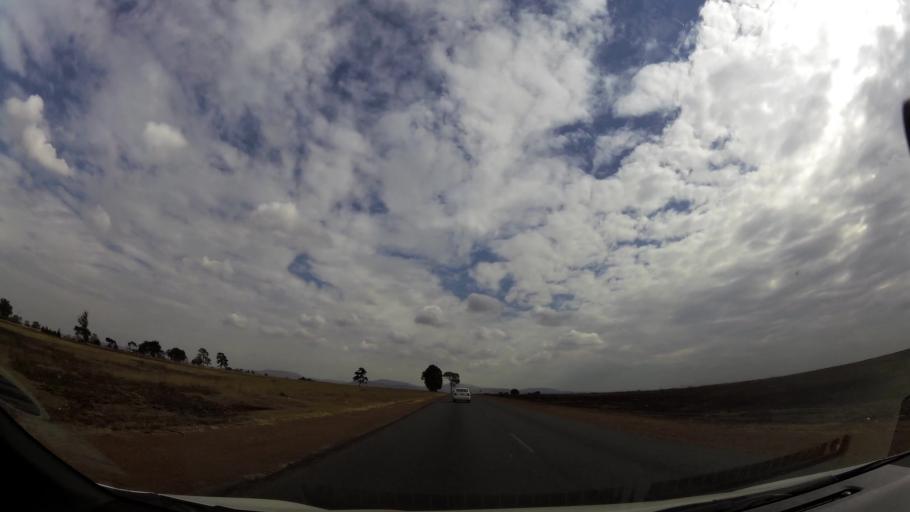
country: ZA
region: Gauteng
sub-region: Sedibeng District Municipality
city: Meyerton
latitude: -26.4212
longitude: 28.1273
